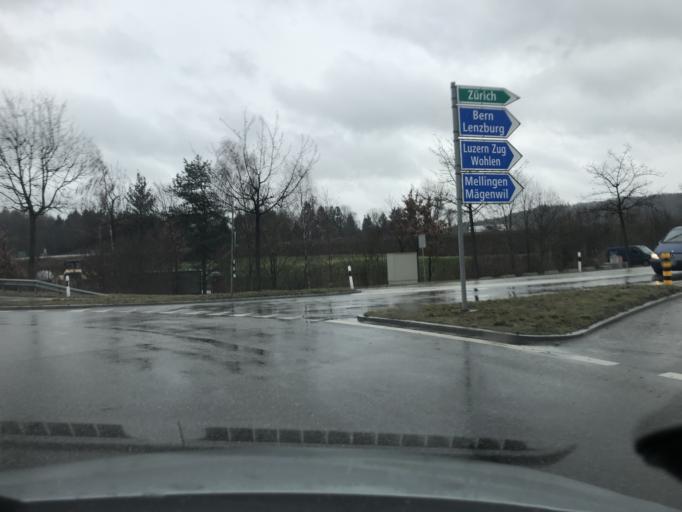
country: CH
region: Aargau
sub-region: Bezirk Lenzburg
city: Othmarsingen
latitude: 47.4212
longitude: 8.2230
